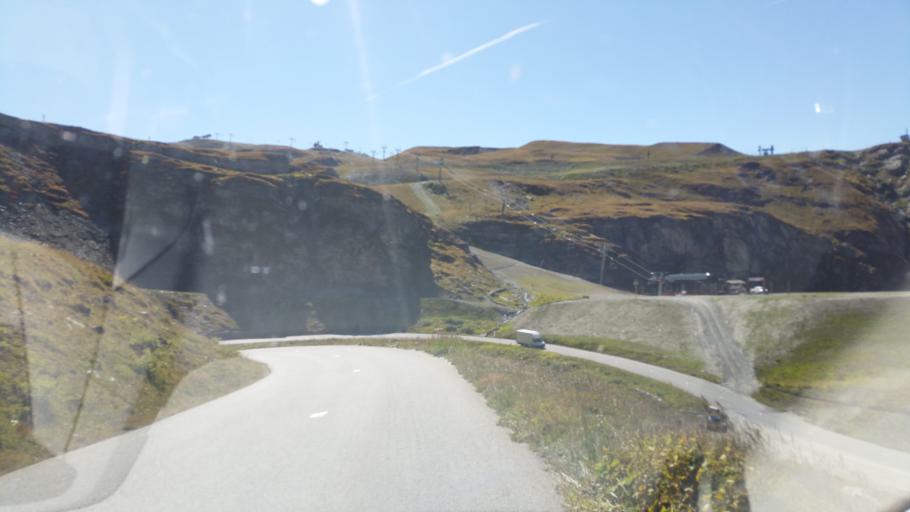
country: FR
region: Rhone-Alpes
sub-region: Departement de la Savoie
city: Val-d'Isere
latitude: 45.4327
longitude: 7.0032
